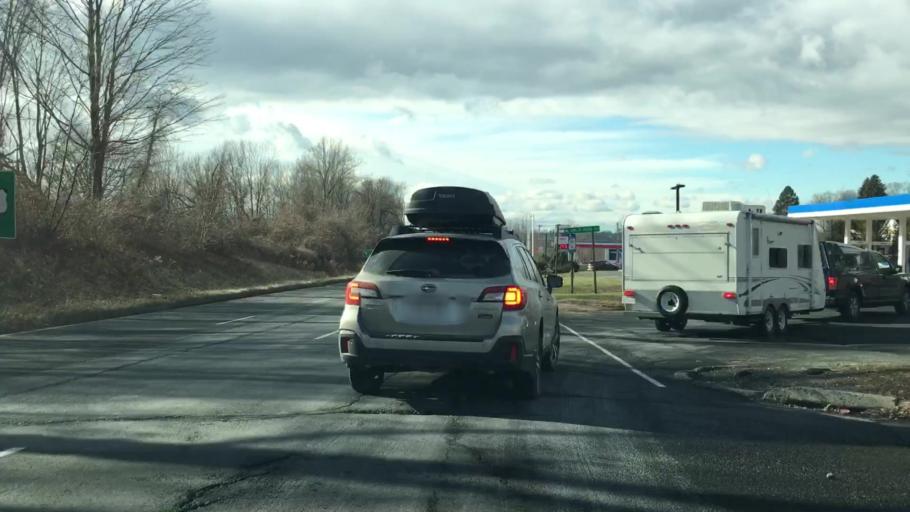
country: US
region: Connecticut
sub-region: Fairfield County
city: Bethel
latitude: 41.4197
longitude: -73.4053
